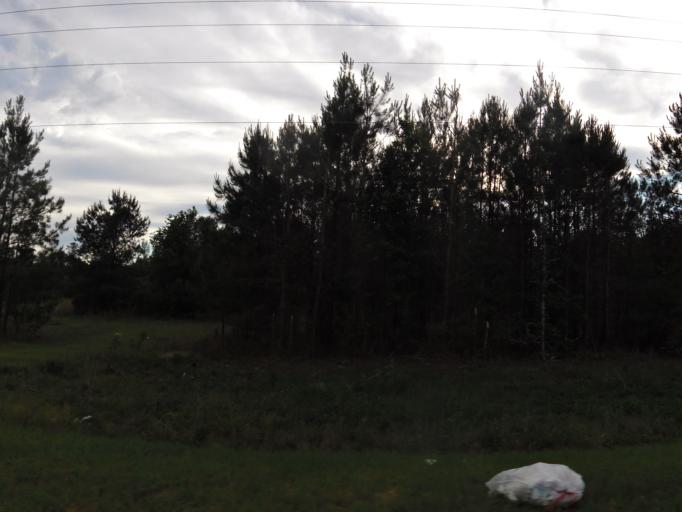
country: US
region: South Carolina
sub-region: Jasper County
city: Hardeeville
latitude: 32.3087
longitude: -81.0877
